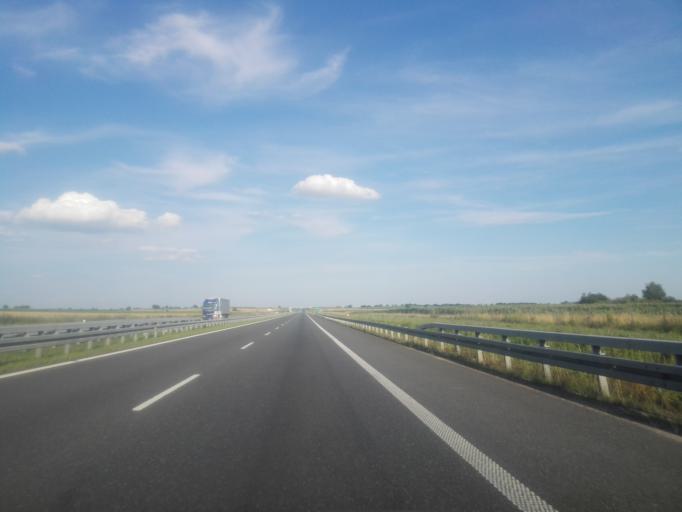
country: PL
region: Lower Silesian Voivodeship
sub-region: Powiat olesnicki
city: Sycow
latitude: 51.3029
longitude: 17.6334
